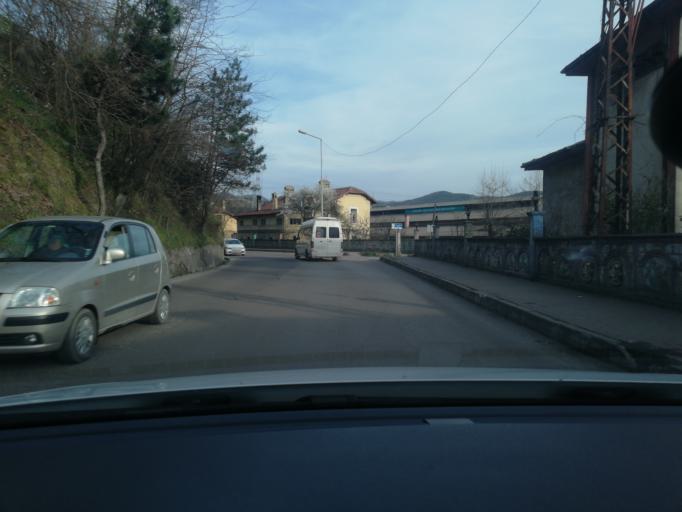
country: TR
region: Zonguldak
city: Kilimli
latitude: 41.5000
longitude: 31.8759
